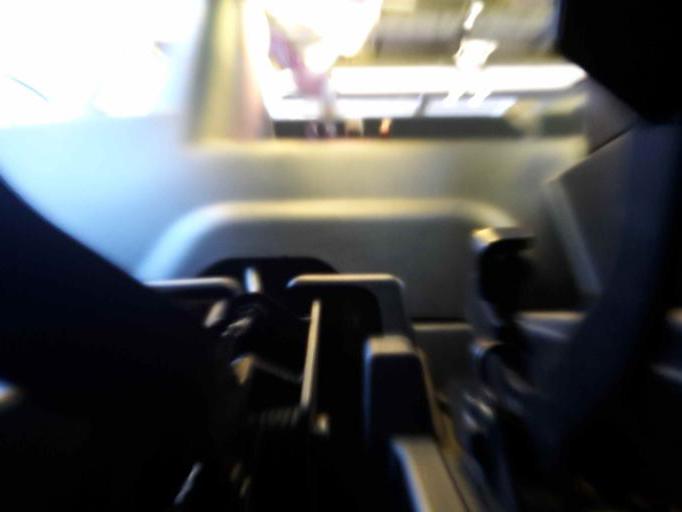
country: BO
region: Cochabamba
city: Sipe Sipe
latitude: -17.5479
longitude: -66.2528
